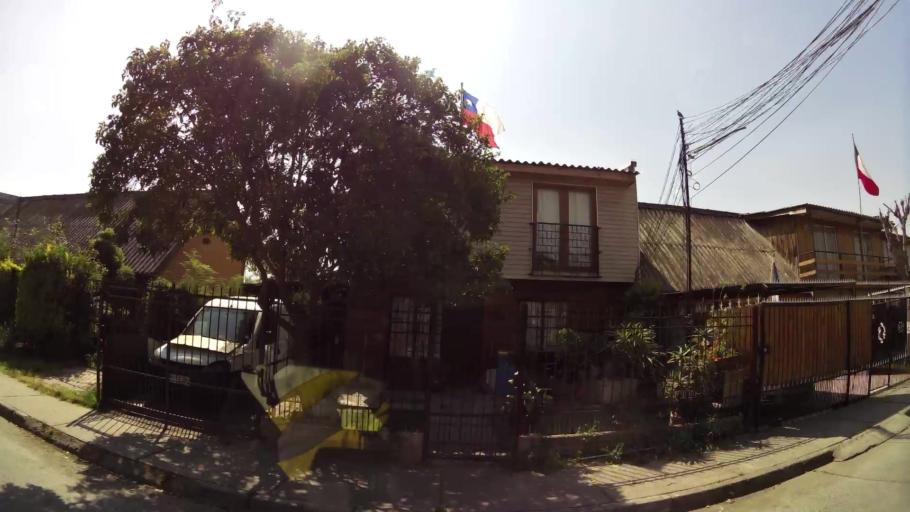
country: CL
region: Santiago Metropolitan
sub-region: Provincia de Santiago
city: La Pintana
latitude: -33.5493
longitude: -70.6092
